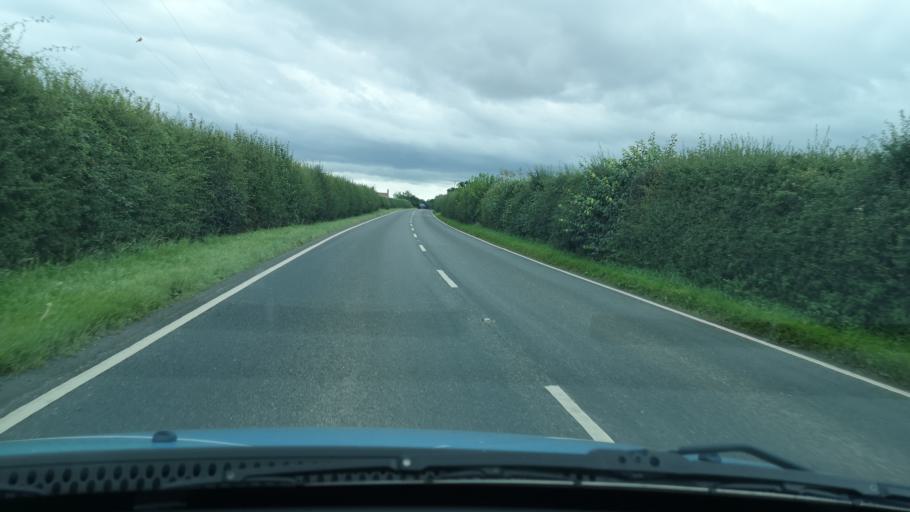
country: GB
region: England
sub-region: City and Borough of Wakefield
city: Featherstone
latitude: 53.6605
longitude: -1.3565
